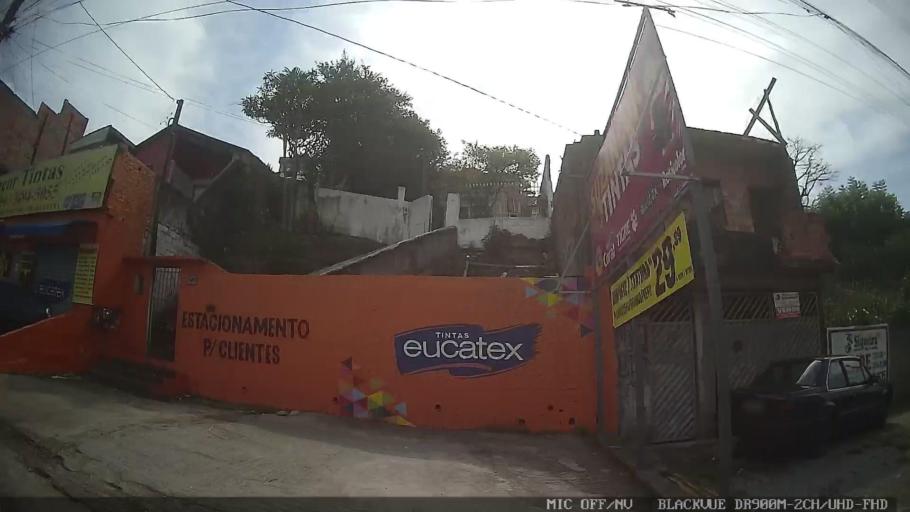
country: BR
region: Sao Paulo
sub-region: Suzano
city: Suzano
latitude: -23.5126
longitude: -46.3002
